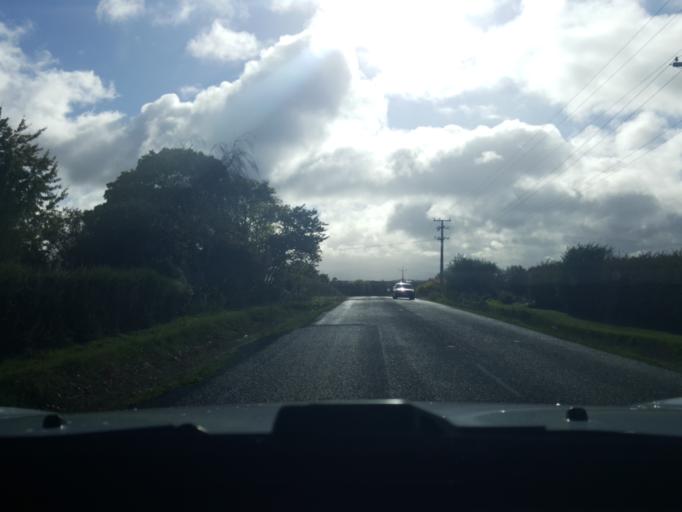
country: NZ
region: Auckland
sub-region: Auckland
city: Pukekohe East
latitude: -37.3082
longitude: 175.0103
